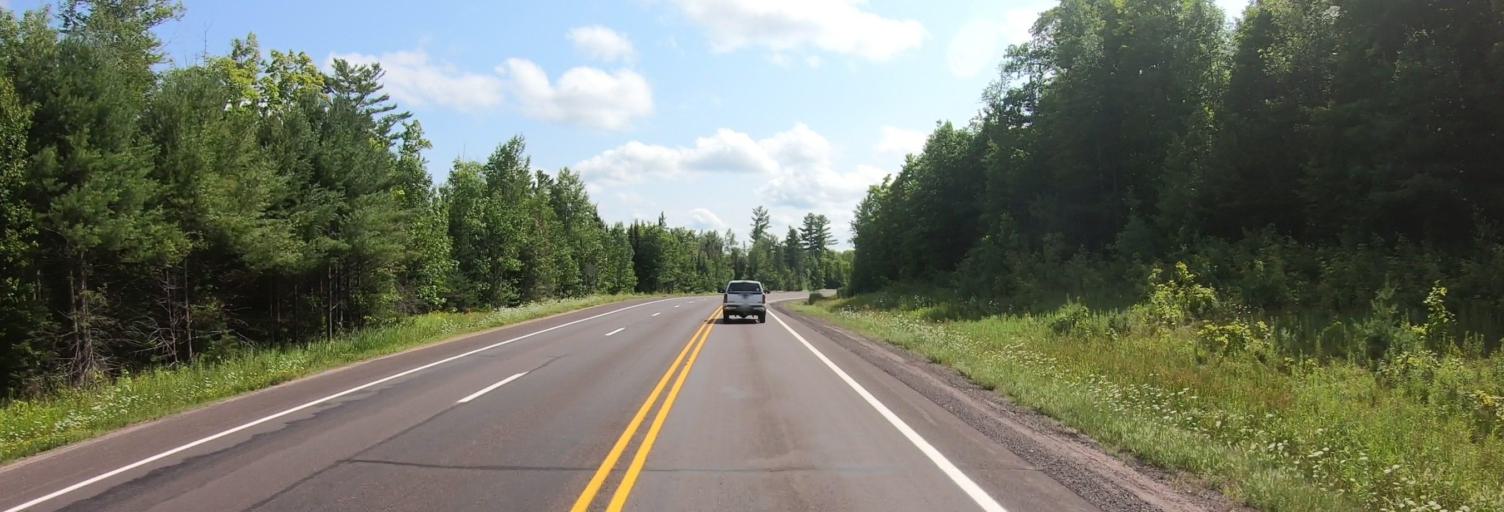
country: US
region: Michigan
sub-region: Ontonagon County
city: Ontonagon
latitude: 46.8102
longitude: -88.9963
